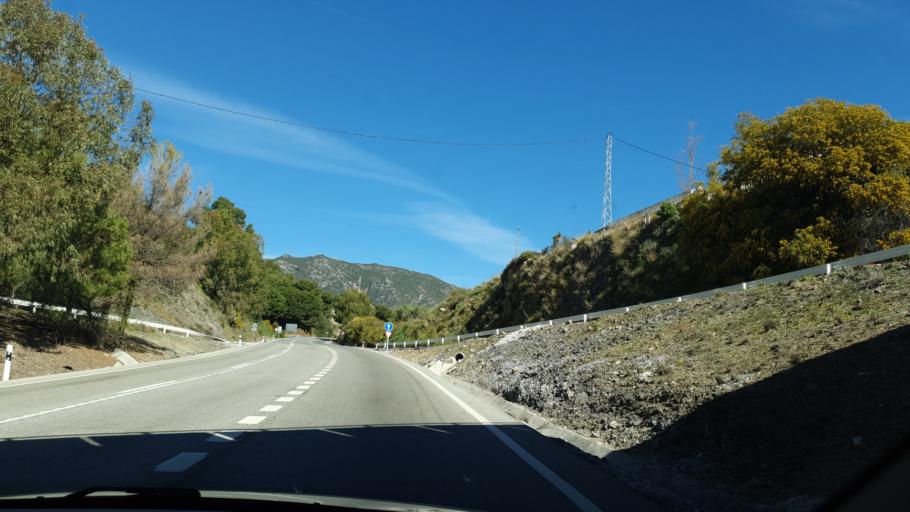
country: ES
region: Andalusia
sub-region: Provincia de Malaga
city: Ojen
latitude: 36.5482
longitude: -4.8613
